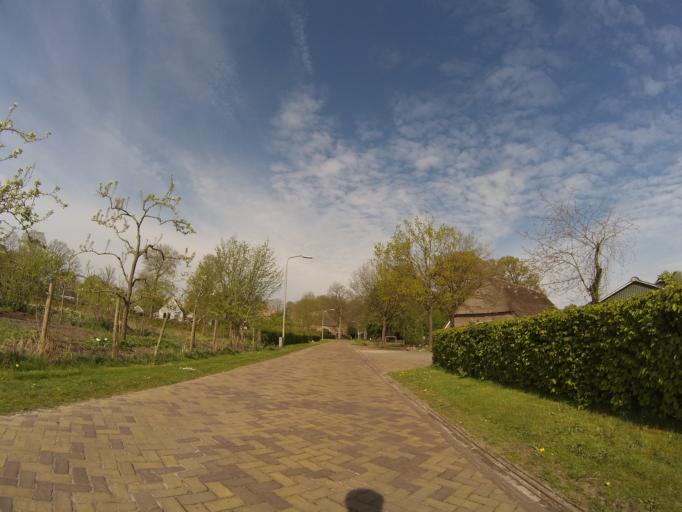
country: NL
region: Drenthe
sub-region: Gemeente Coevorden
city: Sleen
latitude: 52.7937
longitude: 6.7329
